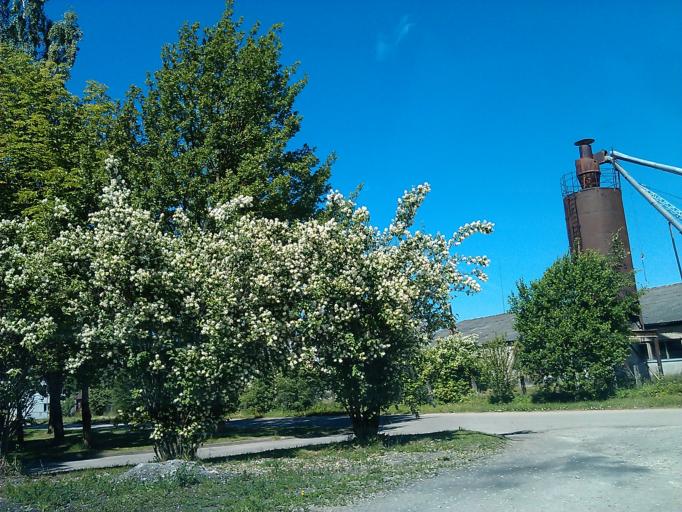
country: LV
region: Vilanu
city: Vilani
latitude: 56.5449
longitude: 26.9336
